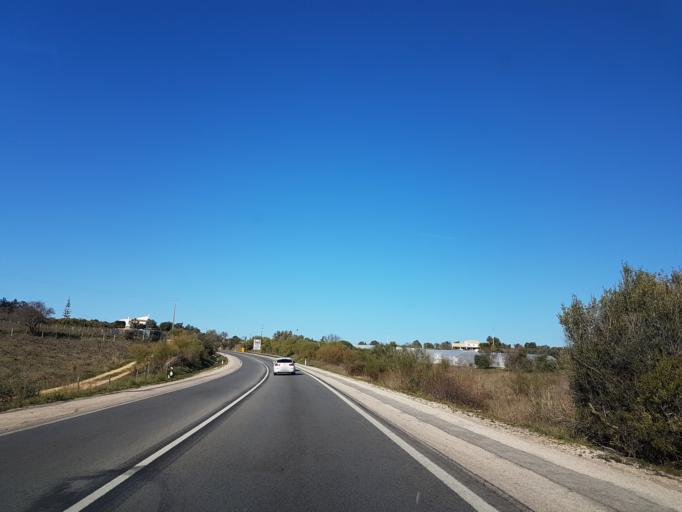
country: PT
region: Faro
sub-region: Lagoa
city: Estombar
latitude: 37.1492
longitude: -8.4797
